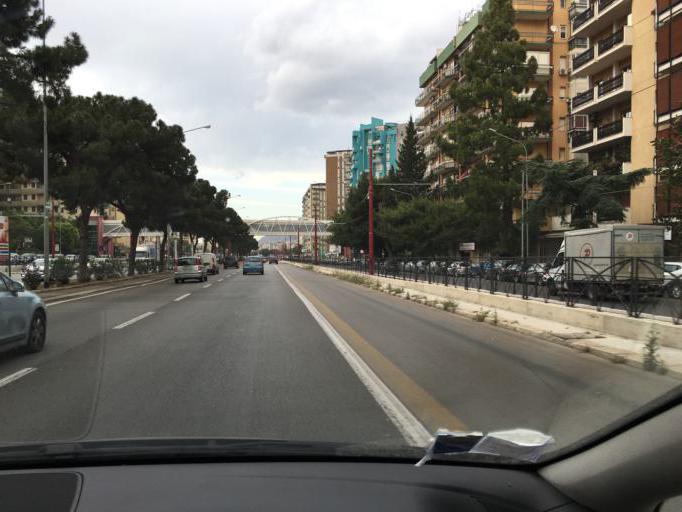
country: IT
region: Sicily
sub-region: Palermo
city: Palermo
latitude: 38.1238
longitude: 13.3293
